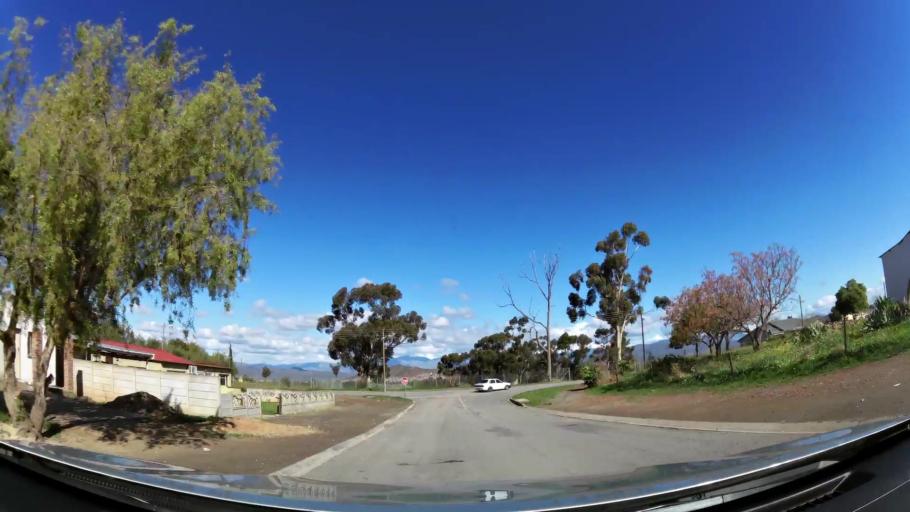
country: ZA
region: Western Cape
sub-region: Cape Winelands District Municipality
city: Ashton
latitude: -33.7919
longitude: 19.8978
